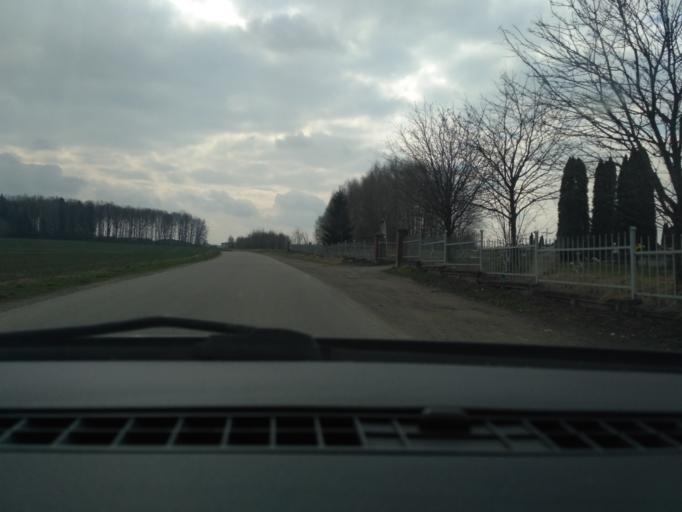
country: PL
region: Subcarpathian Voivodeship
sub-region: Powiat krosnienski
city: Kroscienko Wyzne
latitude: 49.6716
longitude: 21.8276
